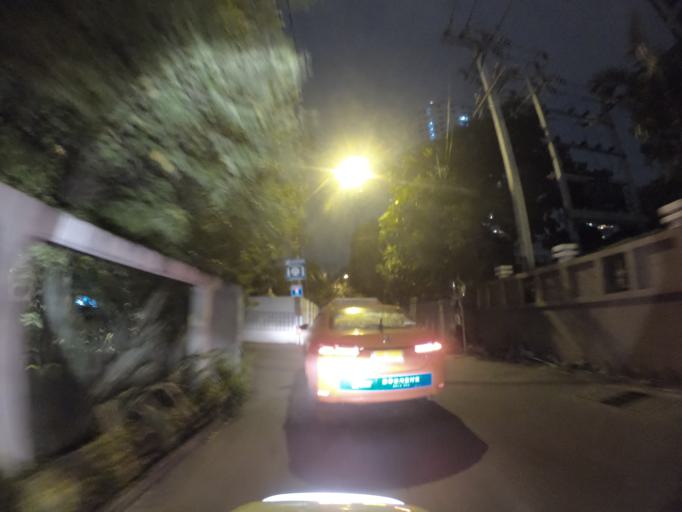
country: TH
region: Bangkok
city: Watthana
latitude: 13.7415
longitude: 100.5697
